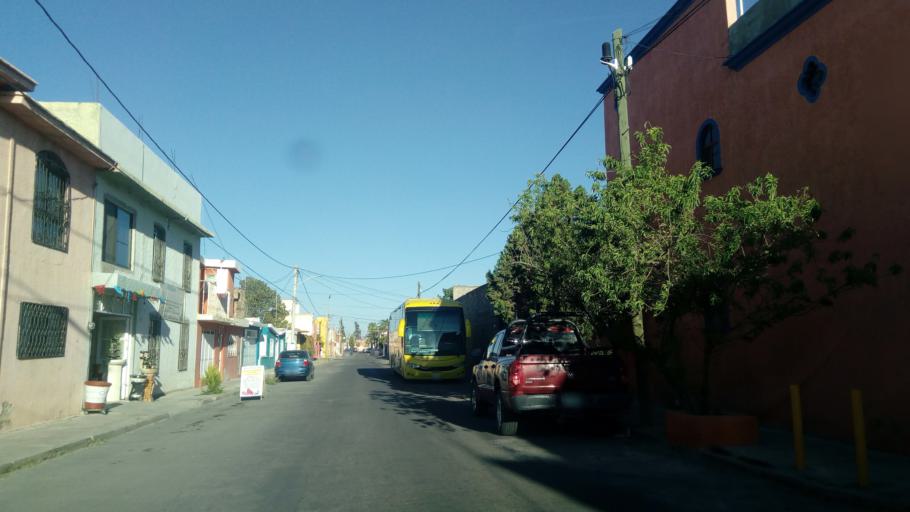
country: MX
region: Durango
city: Victoria de Durango
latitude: 24.0117
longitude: -104.6815
